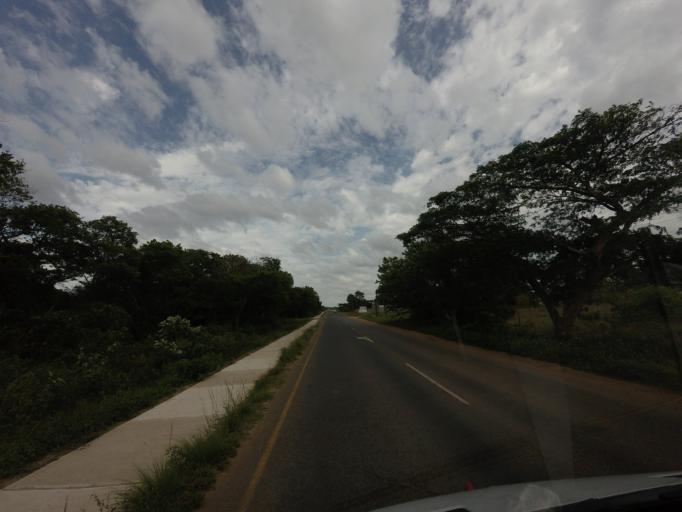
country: ZA
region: KwaZulu-Natal
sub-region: uMkhanyakude District Municipality
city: Mtubatuba
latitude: -28.3755
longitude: 32.3802
